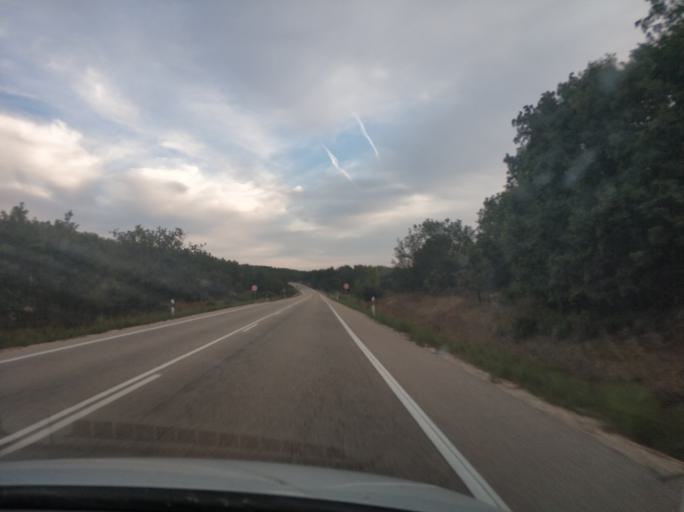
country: ES
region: Castille and Leon
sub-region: Provincia de Burgos
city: Pinilla de los Barruecos
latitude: 41.9218
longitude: -3.2793
